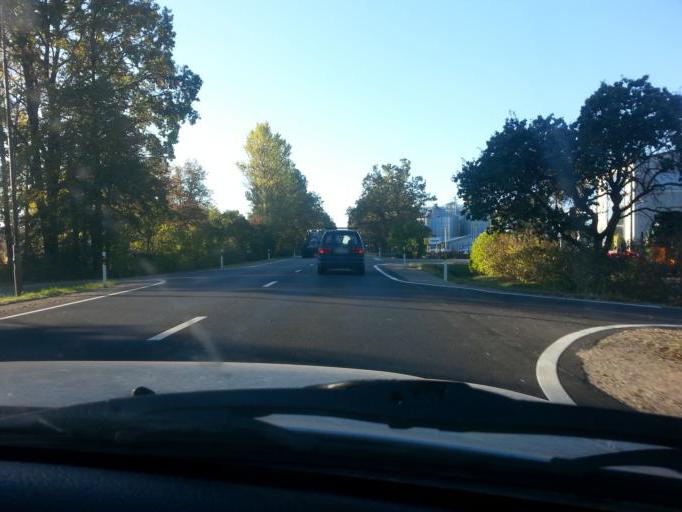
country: LT
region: Siauliu apskritis
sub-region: Joniskis
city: Joniskis
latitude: 56.4221
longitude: 23.6847
